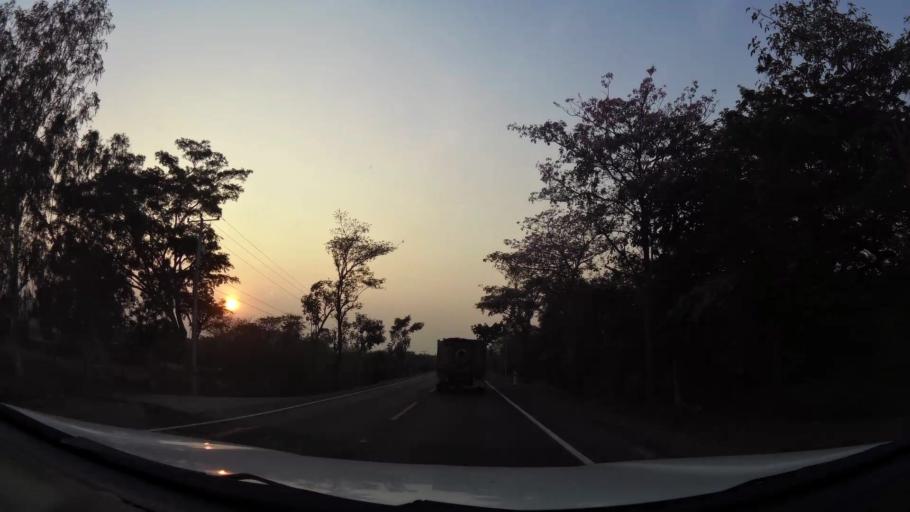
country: NI
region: Leon
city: La Paz Centro
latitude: 12.3103
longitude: -86.7832
